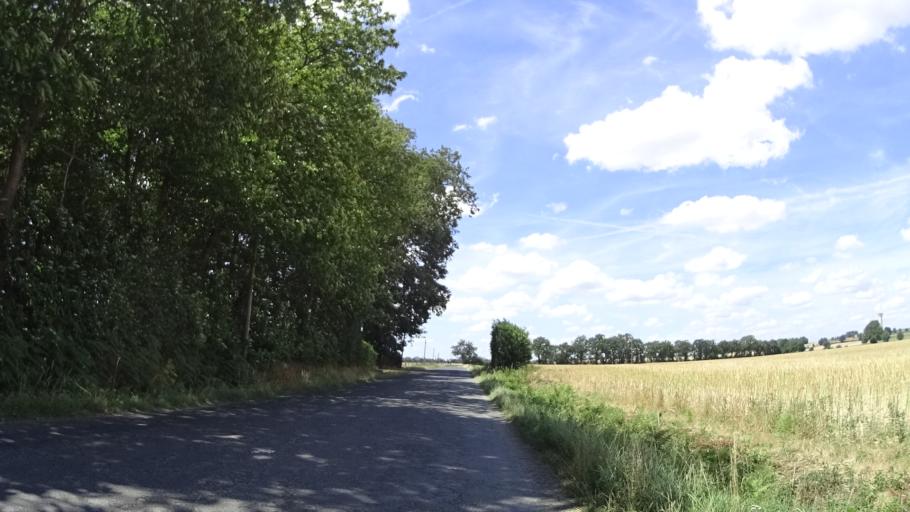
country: FR
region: Pays de la Loire
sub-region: Departement de Maine-et-Loire
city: Noyant-la-Gravoyere
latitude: 47.6146
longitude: -0.9451
